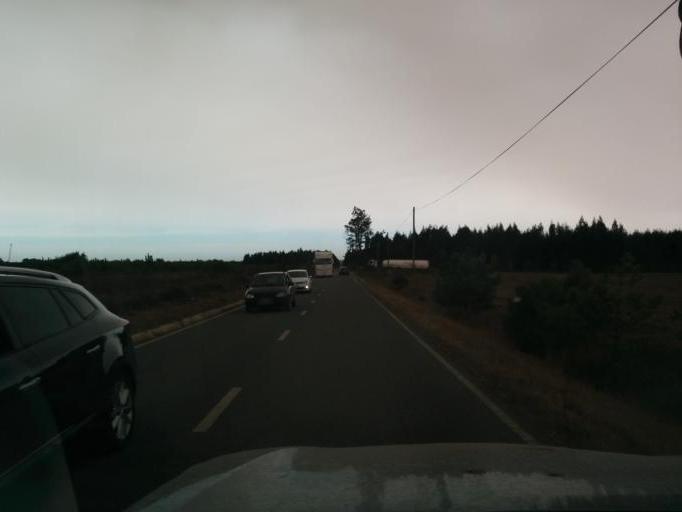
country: PT
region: Beja
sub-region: Odemira
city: Sao Teotonio
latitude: 37.5559
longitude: -8.7350
